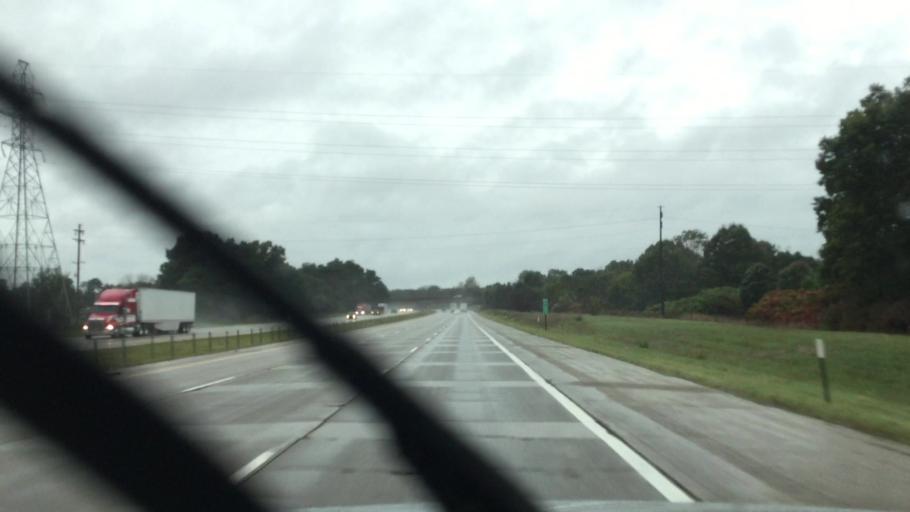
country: US
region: Michigan
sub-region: Berrien County
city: Fair Plain
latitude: 42.0543
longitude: -86.4789
